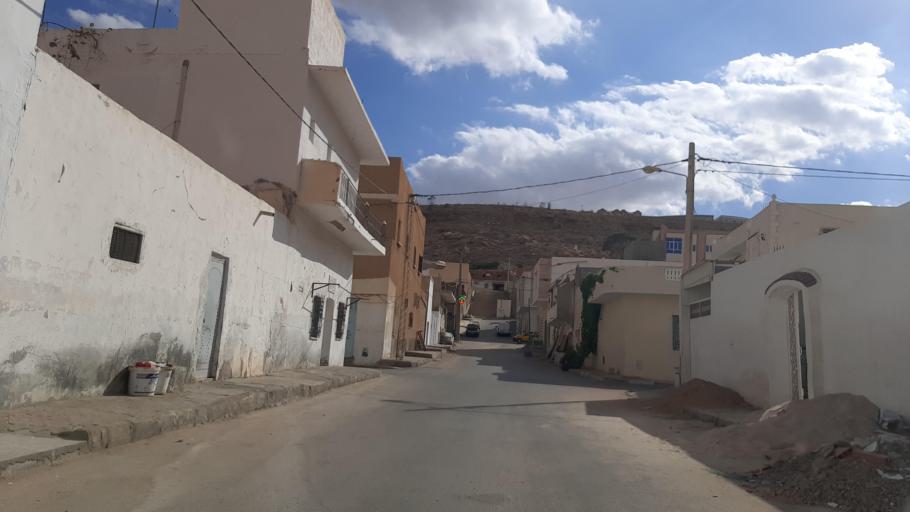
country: TN
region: Tataouine
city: Tataouine
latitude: 32.9265
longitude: 10.4528
